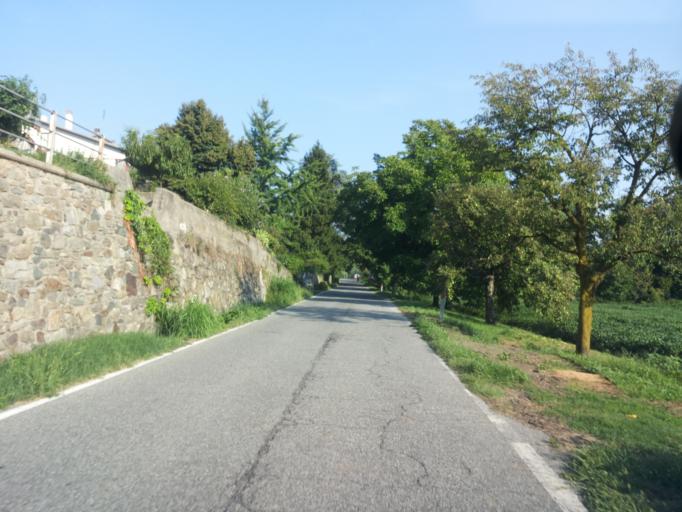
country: IT
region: Piedmont
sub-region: Provincia di Torino
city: Palazzo Canavese
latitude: 45.4633
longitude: 7.9683
